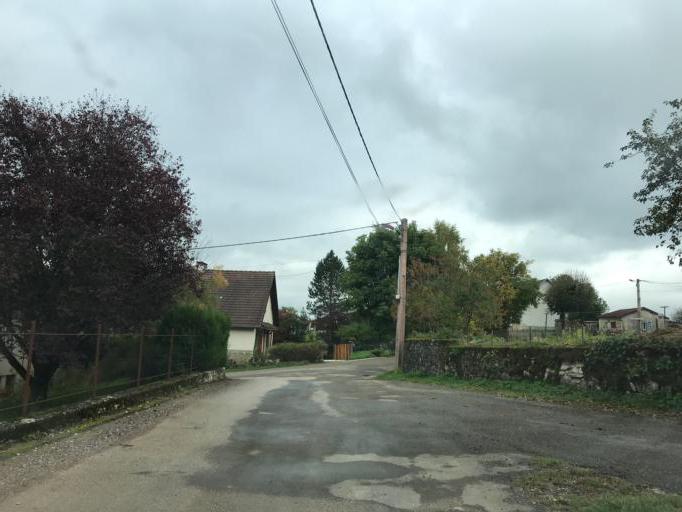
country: FR
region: Franche-Comte
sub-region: Departement du Jura
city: Arinthod
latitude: 46.4417
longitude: 5.5515
